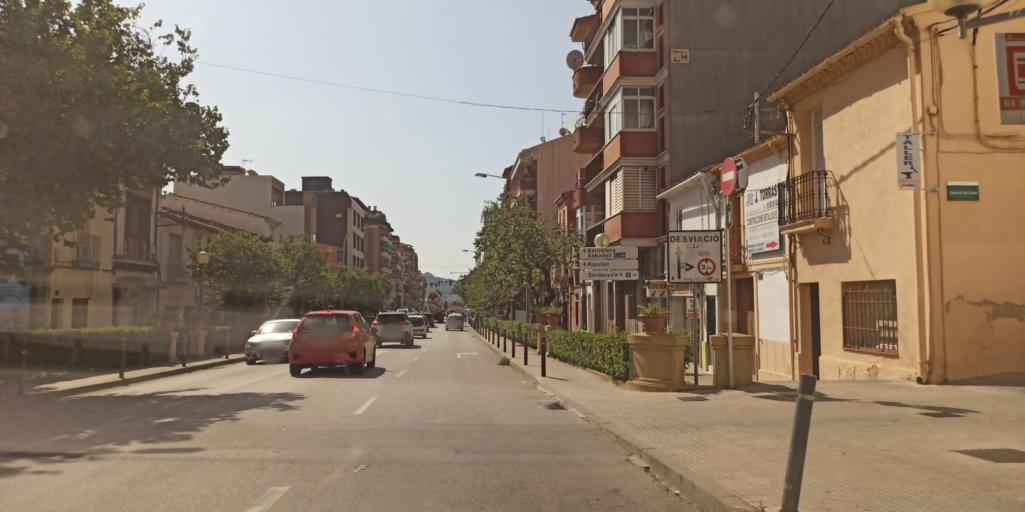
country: ES
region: Catalonia
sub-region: Provincia de Barcelona
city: Cerdanyola del Valles
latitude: 41.4940
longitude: 2.1470
